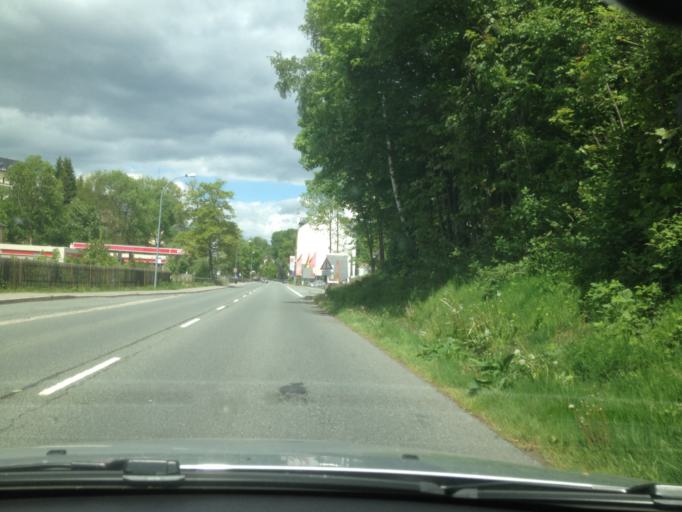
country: DE
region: Saxony
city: Annaberg-Buchholz
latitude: 50.5654
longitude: 12.9987
